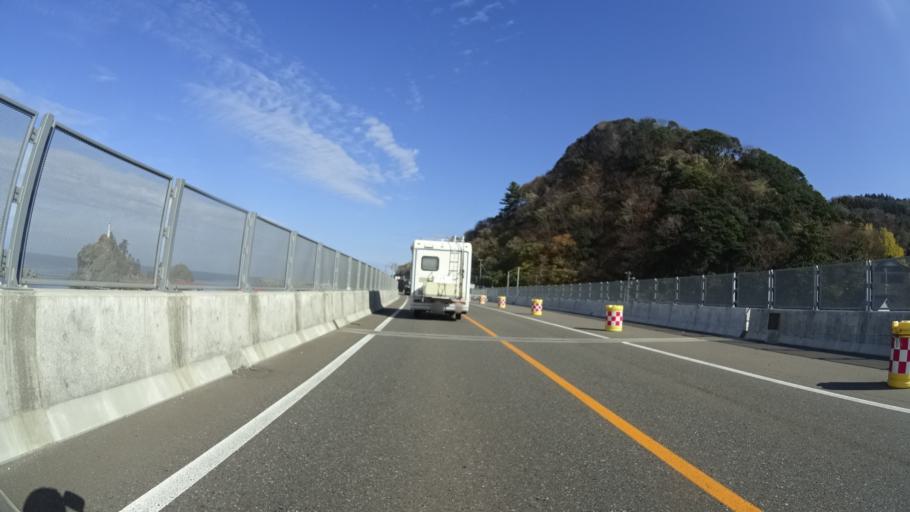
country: JP
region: Niigata
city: Itoigawa
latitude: 37.1071
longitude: 137.9928
